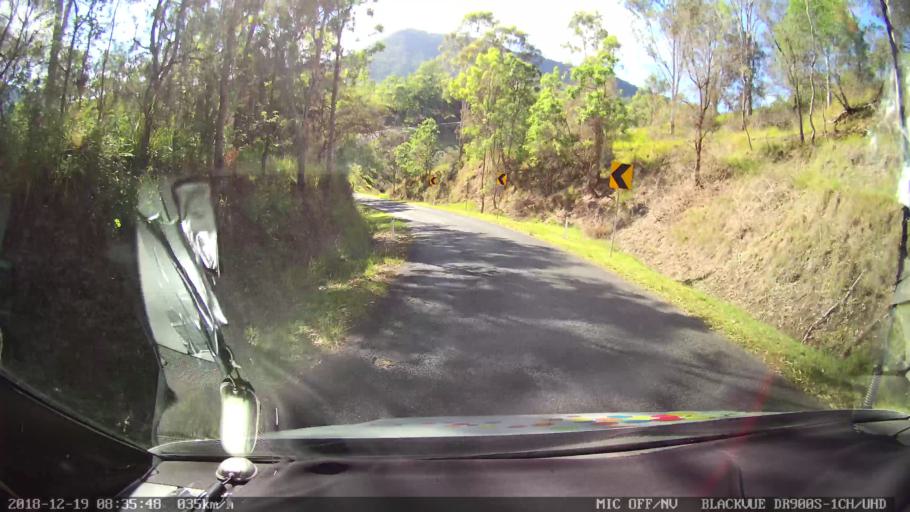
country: AU
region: New South Wales
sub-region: Kyogle
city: Kyogle
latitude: -28.3227
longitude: 152.9715
